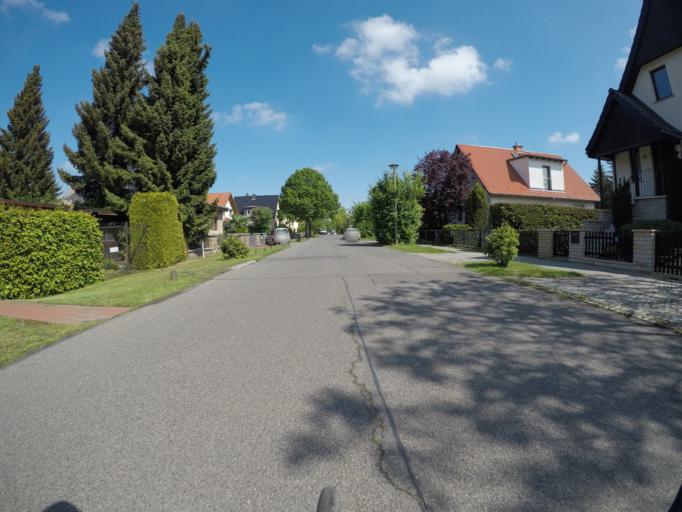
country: DE
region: Berlin
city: Biesdorf
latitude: 52.5170
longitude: 13.5481
